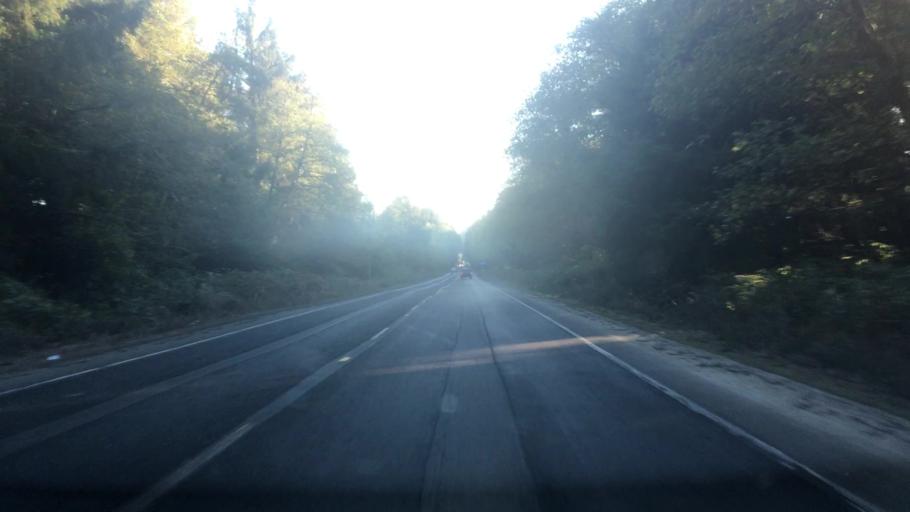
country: US
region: Oregon
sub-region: Clatsop County
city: Cannon Beach
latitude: 45.8969
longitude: -123.9548
